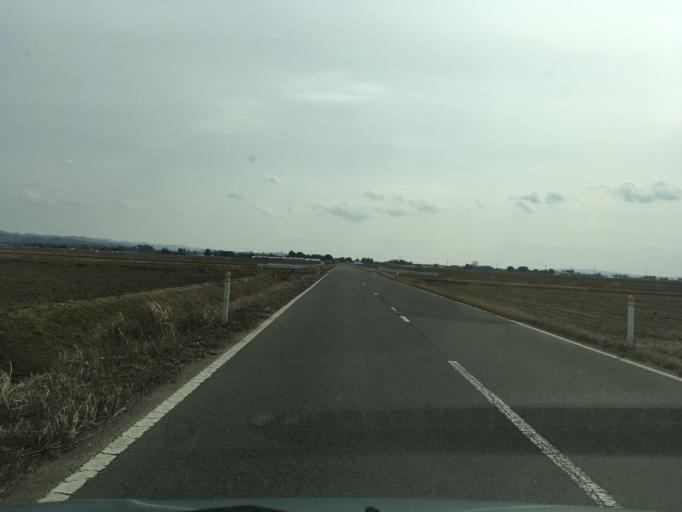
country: JP
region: Iwate
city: Ichinoseki
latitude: 38.7343
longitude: 141.2389
